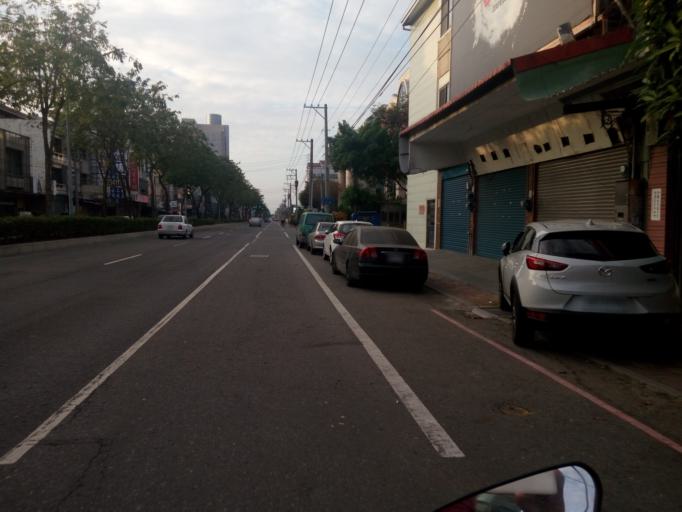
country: TW
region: Taiwan
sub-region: Chiayi
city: Jiayi Shi
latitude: 23.4785
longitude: 120.4329
